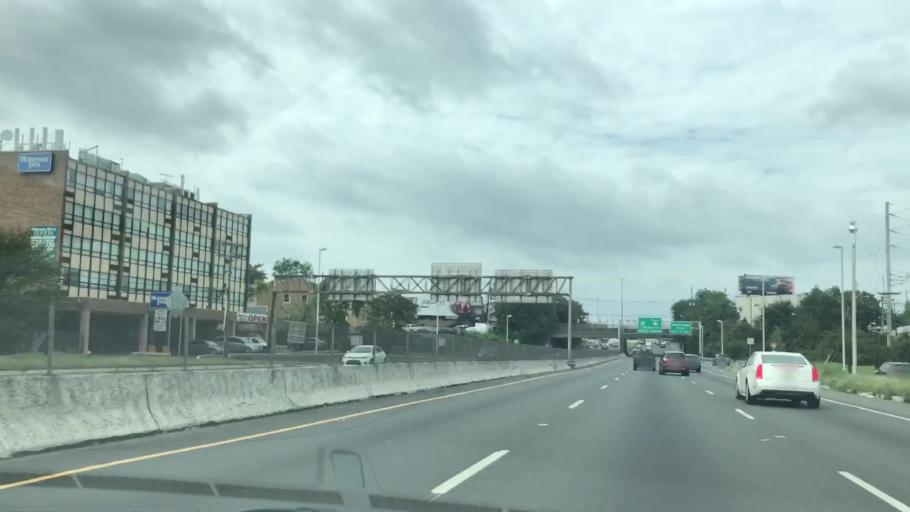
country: US
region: New Jersey
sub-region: Hudson County
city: Secaucus
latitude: 40.7929
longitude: -74.0563
